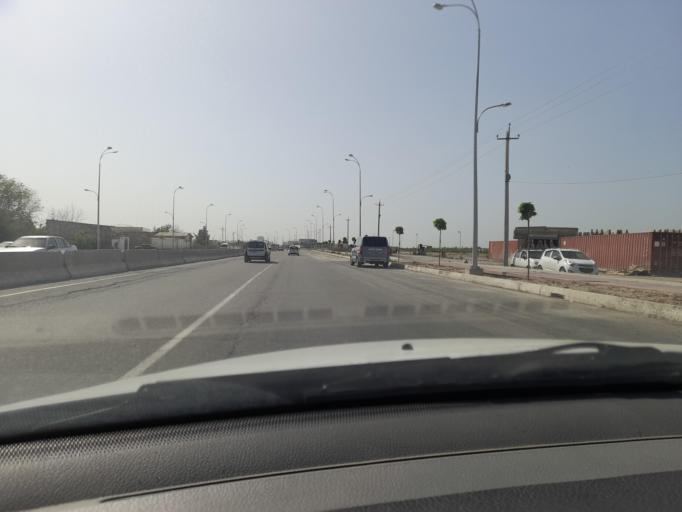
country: UZ
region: Samarqand
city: Samarqand
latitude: 39.7108
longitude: 66.9794
